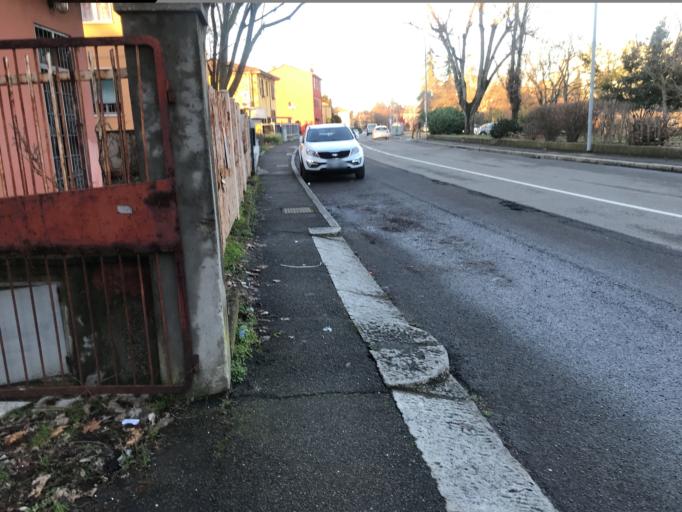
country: IT
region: Emilia-Romagna
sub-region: Provincia di Bologna
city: Progresso
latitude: 44.5402
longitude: 11.3512
